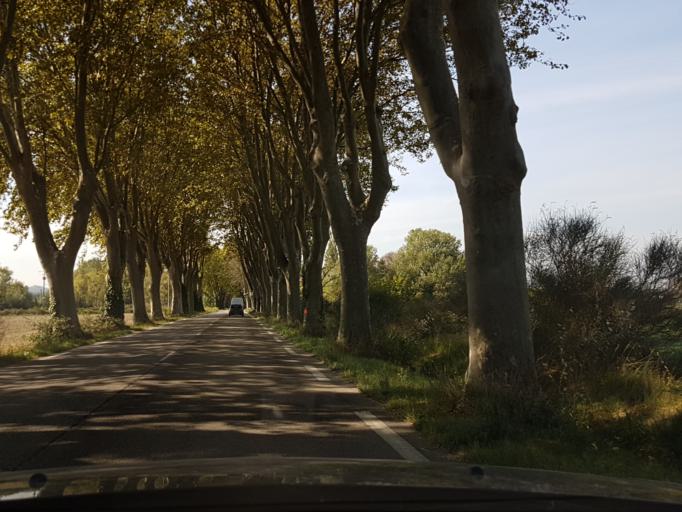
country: FR
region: Provence-Alpes-Cote d'Azur
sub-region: Departement des Bouches-du-Rhone
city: Molleges
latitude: 43.7844
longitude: 4.9037
